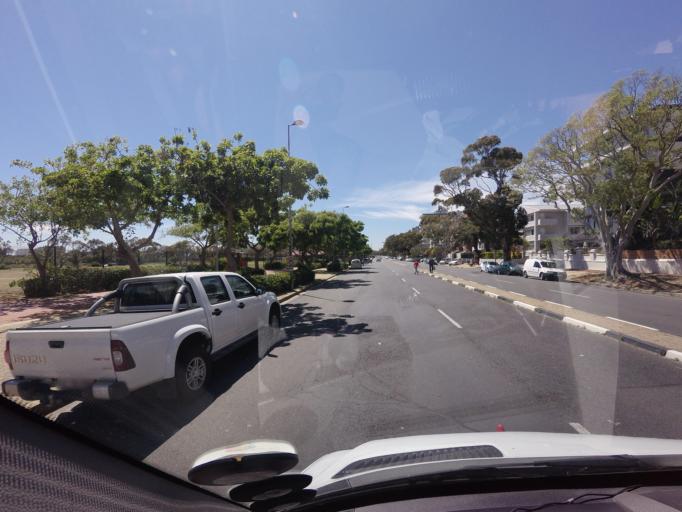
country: ZA
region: Western Cape
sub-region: City of Cape Town
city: Cape Town
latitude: -33.9078
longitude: 18.4019
